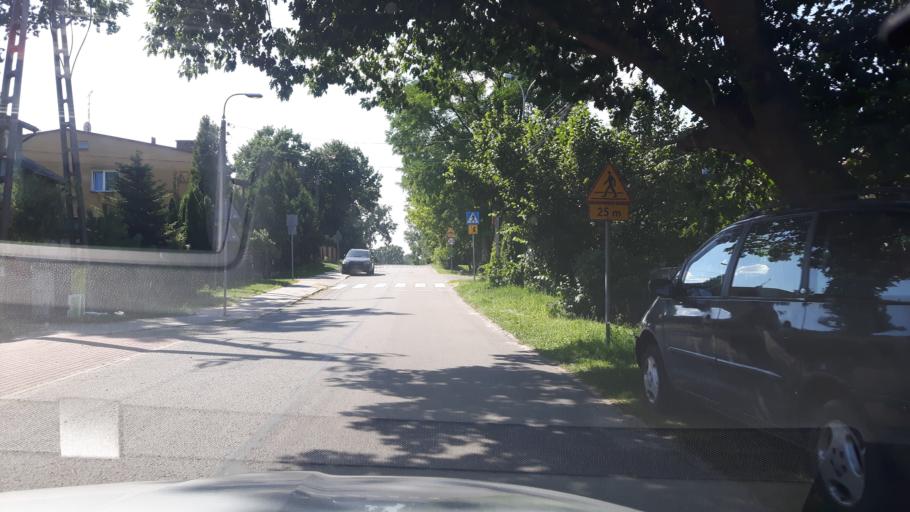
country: PL
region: Masovian Voivodeship
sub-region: Warszawa
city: Rembertow
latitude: 52.2447
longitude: 21.1859
